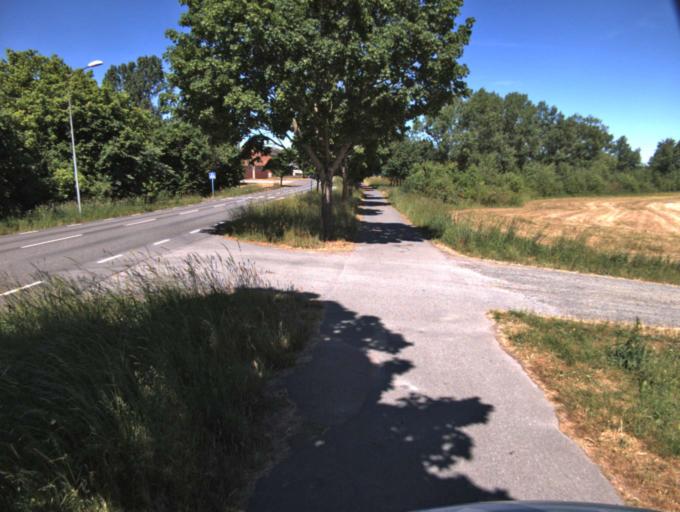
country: SE
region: Skane
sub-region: Kristianstads Kommun
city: Onnestad
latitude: 56.0517
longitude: 14.0227
